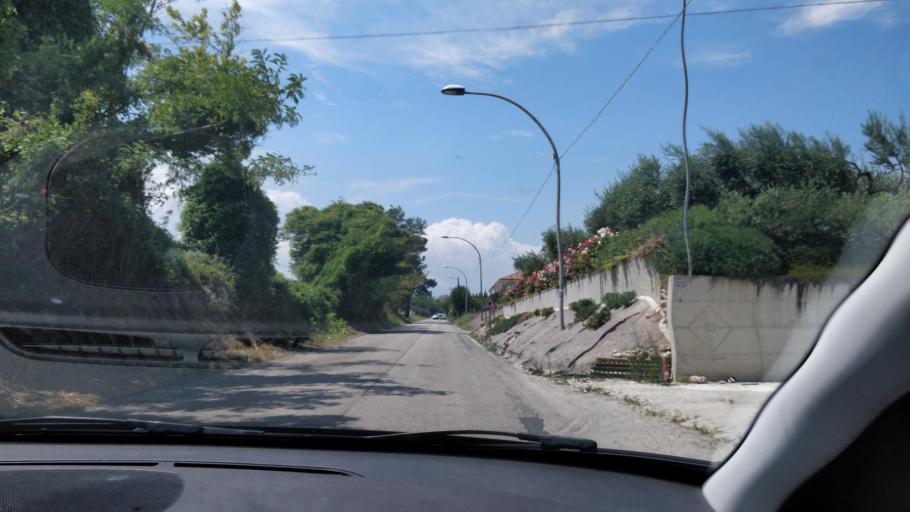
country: IT
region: Abruzzo
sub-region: Provincia di Chieti
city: Francavilla al Mare
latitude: 42.4241
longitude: 14.2564
